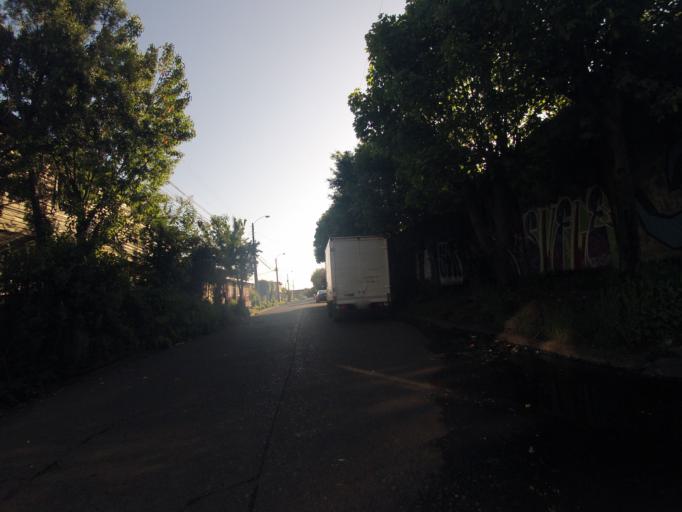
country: CL
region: Araucania
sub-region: Provincia de Cautin
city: Temuco
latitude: -38.7280
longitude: -72.5766
